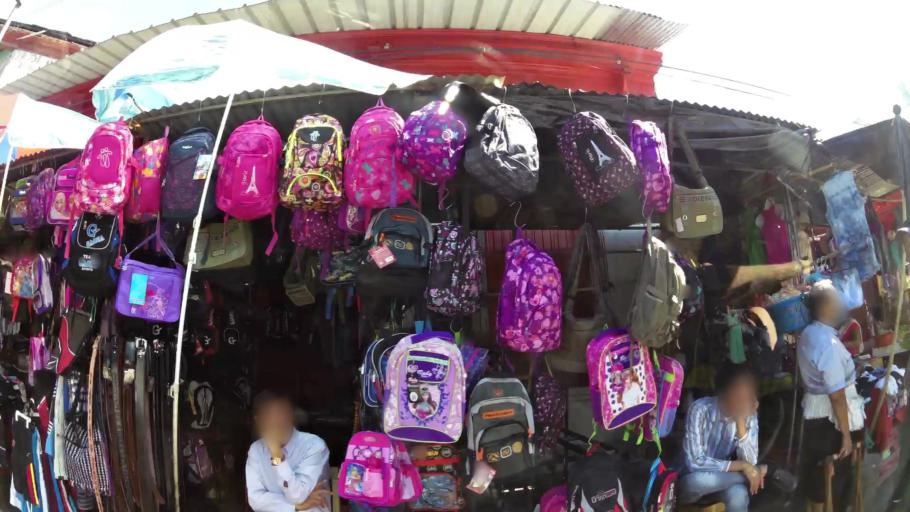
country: SV
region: La Libertad
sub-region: Distrito de Quezaltepeque
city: Quezaltepeque
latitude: 13.8349
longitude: -89.2723
